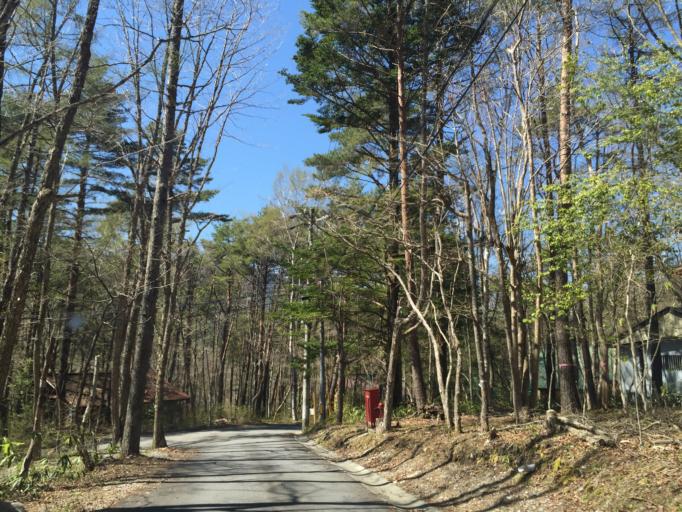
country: JP
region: Gifu
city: Nakatsugawa
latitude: 35.3504
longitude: 137.6723
